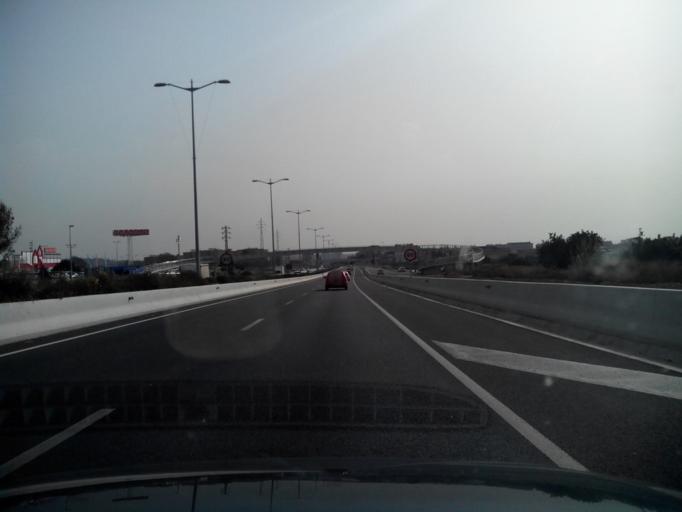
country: ES
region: Catalonia
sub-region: Provincia de Tarragona
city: Constanti
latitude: 41.1272
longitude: 1.2040
